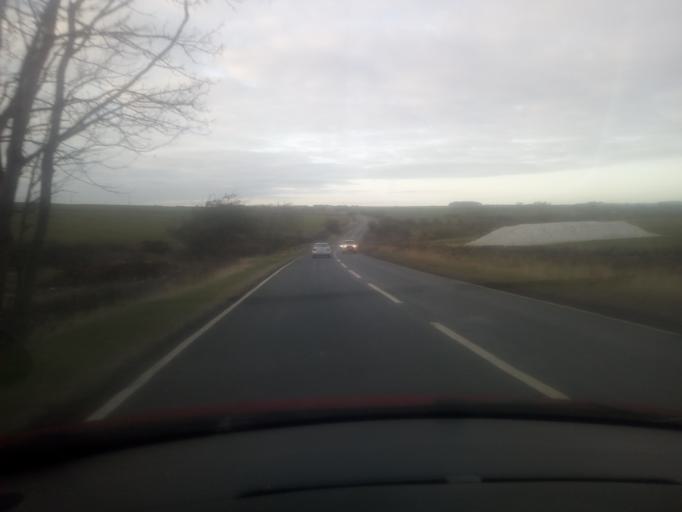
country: GB
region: England
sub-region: County Durham
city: Castleside
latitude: 54.7857
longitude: -1.8564
